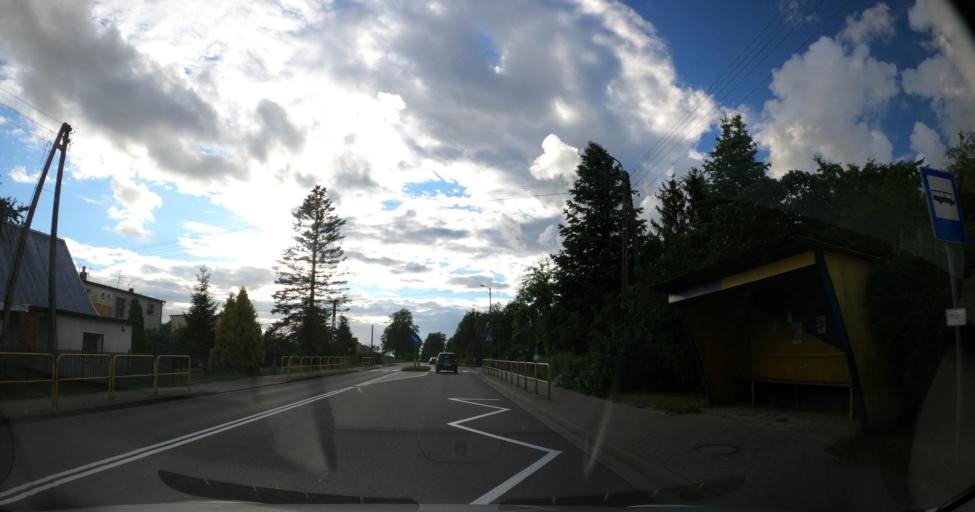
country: PL
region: Pomeranian Voivodeship
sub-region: Powiat slupski
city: Potegowo
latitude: 54.4229
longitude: 17.3789
